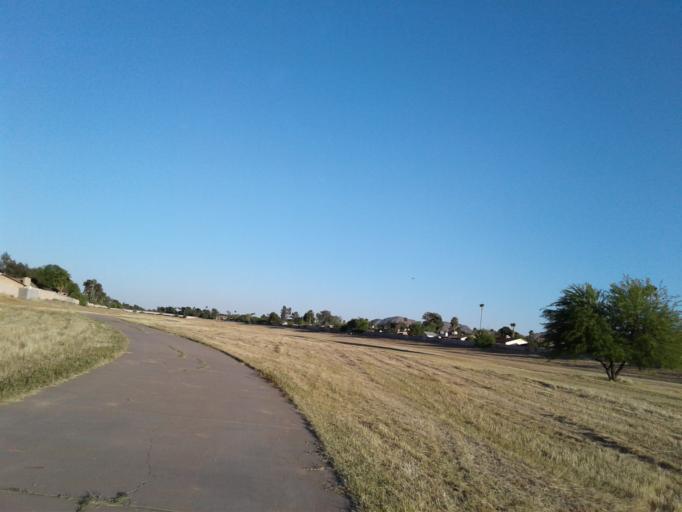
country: US
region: Arizona
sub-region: Maricopa County
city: Paradise Valley
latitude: 33.6033
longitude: -112.0034
